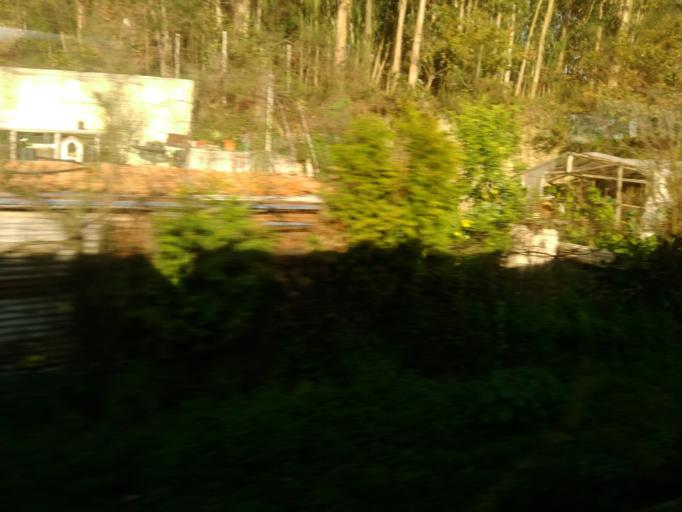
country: PT
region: Braga
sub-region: Braga
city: Oliveira
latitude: 41.5007
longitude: -8.4929
